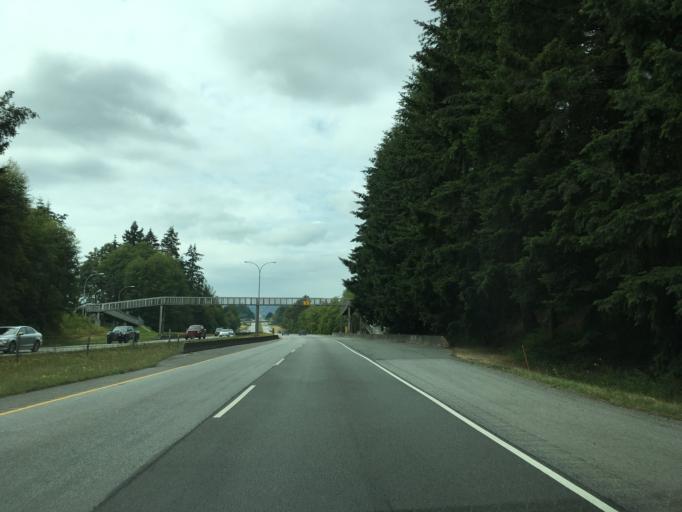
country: CA
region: British Columbia
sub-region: Greater Vancouver Regional District
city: White Rock
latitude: 49.0519
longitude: -122.7923
